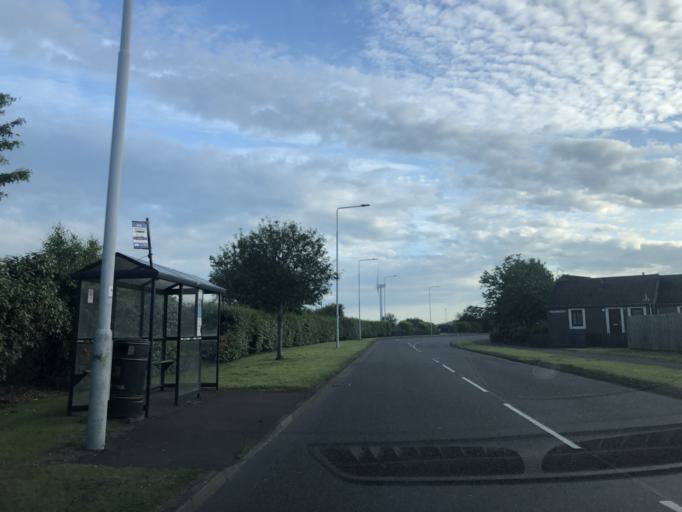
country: GB
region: Scotland
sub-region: Fife
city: Leven
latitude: 56.1844
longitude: -3.0092
